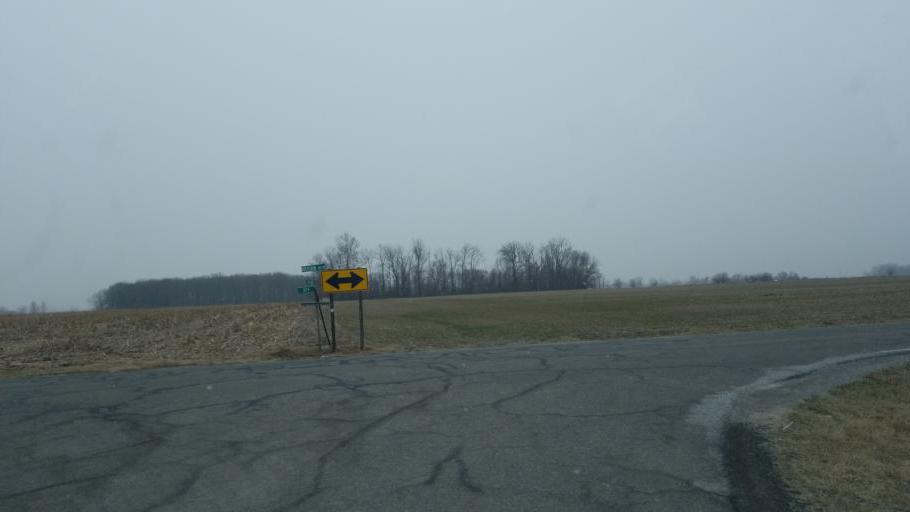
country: US
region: Ohio
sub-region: Defiance County
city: Hicksville
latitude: 41.3251
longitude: -84.7381
